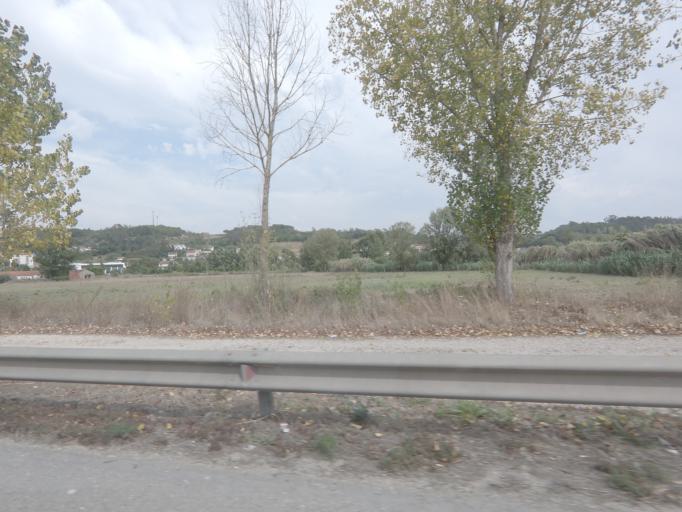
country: PT
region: Leiria
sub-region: Pombal
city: Pombal
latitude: 39.9059
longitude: -8.6335
